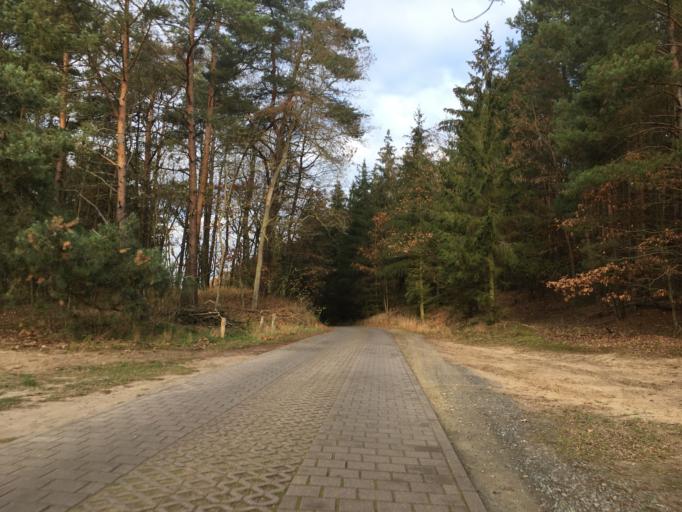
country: DE
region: Brandenburg
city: Buckow
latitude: 52.5646
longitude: 14.1258
